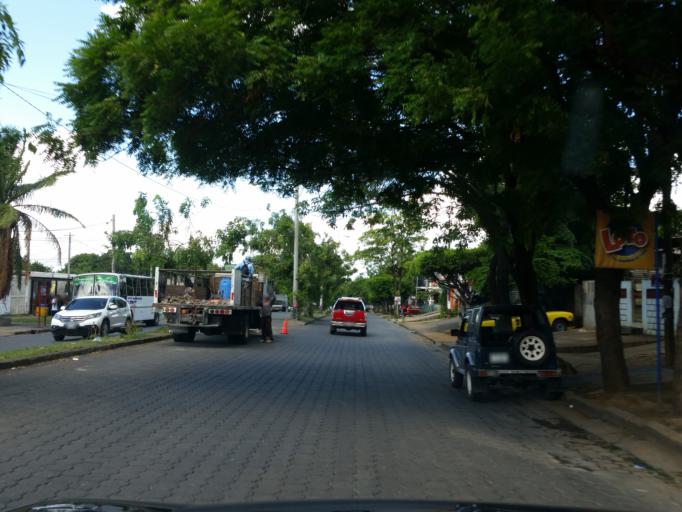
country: NI
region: Managua
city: Managua
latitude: 12.1374
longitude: -86.2167
